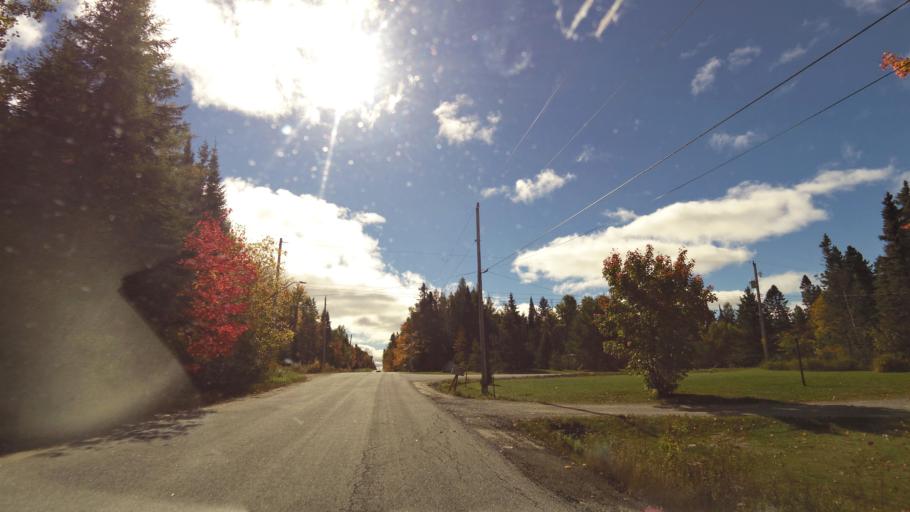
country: CA
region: Ontario
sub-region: Nipissing District
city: North Bay
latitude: 46.3620
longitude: -79.4872
